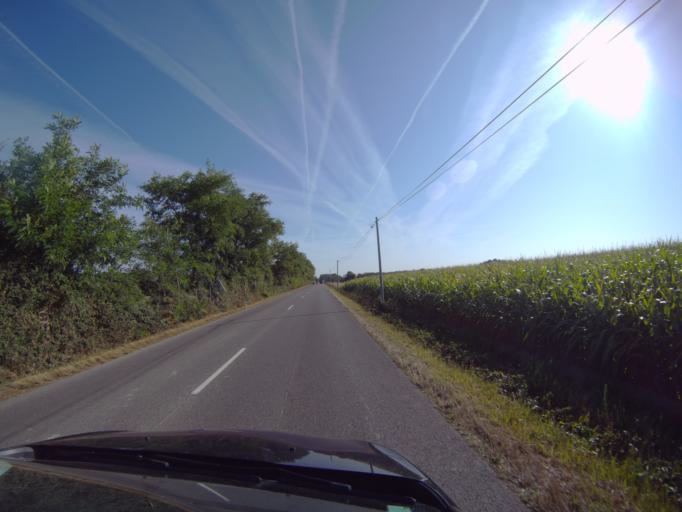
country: FR
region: Pays de la Loire
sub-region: Departement de la Vendee
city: Nieul-le-Dolent
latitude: 46.5356
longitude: -1.5414
